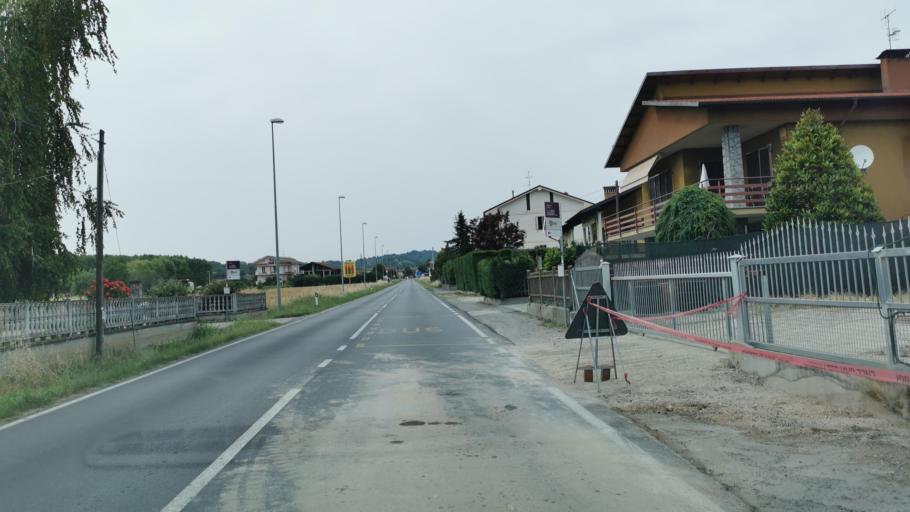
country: IT
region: Piedmont
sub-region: Provincia di Cuneo
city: Pocapaglia
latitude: 44.6926
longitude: 7.8911
